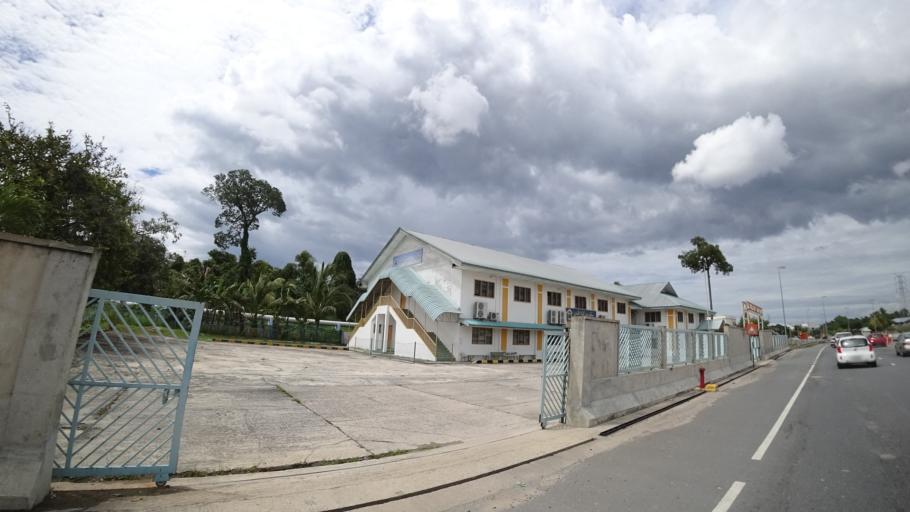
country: BN
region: Brunei and Muara
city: Bandar Seri Begawan
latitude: 4.8833
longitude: 114.8944
